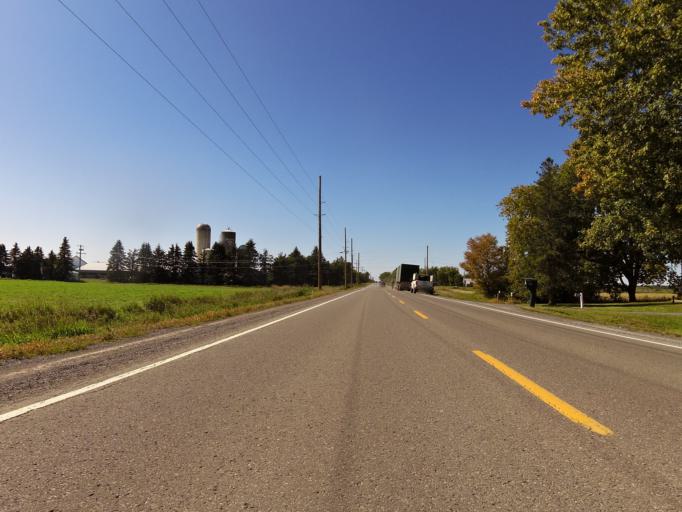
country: CA
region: Ontario
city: Casselman
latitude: 45.2447
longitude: -75.1567
